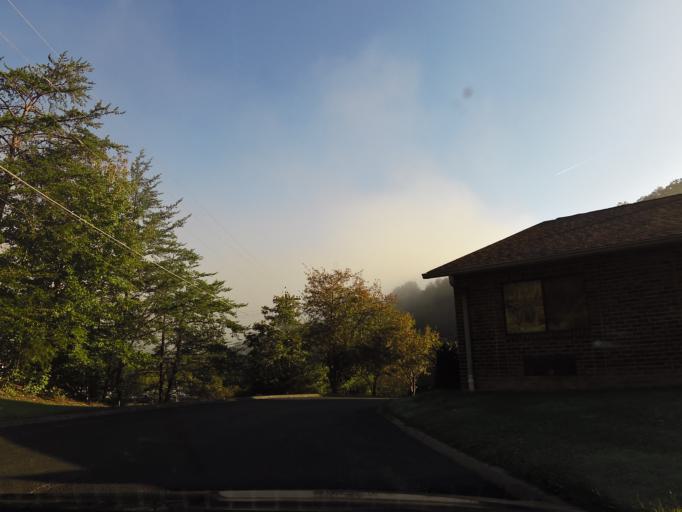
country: US
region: Tennessee
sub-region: Campbell County
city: Jellico
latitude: 36.5724
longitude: -84.1276
